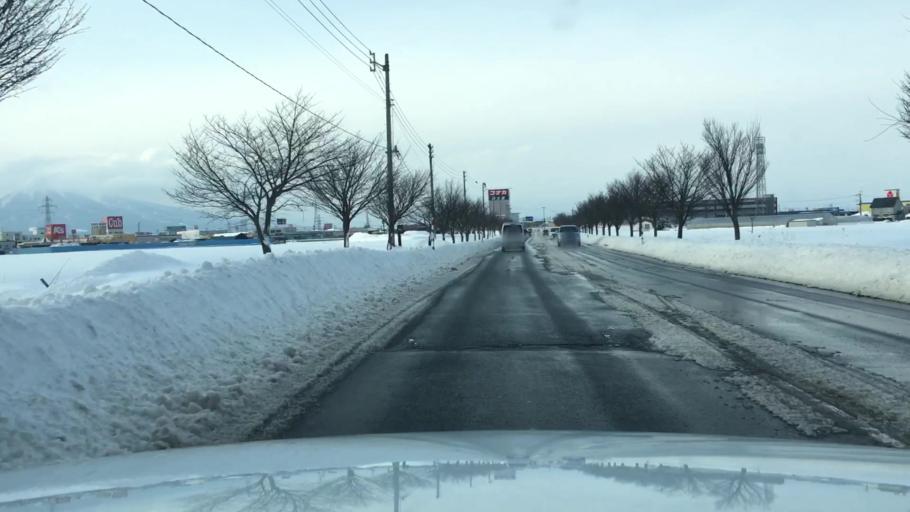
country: JP
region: Aomori
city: Hirosaki
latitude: 40.5954
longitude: 140.5176
